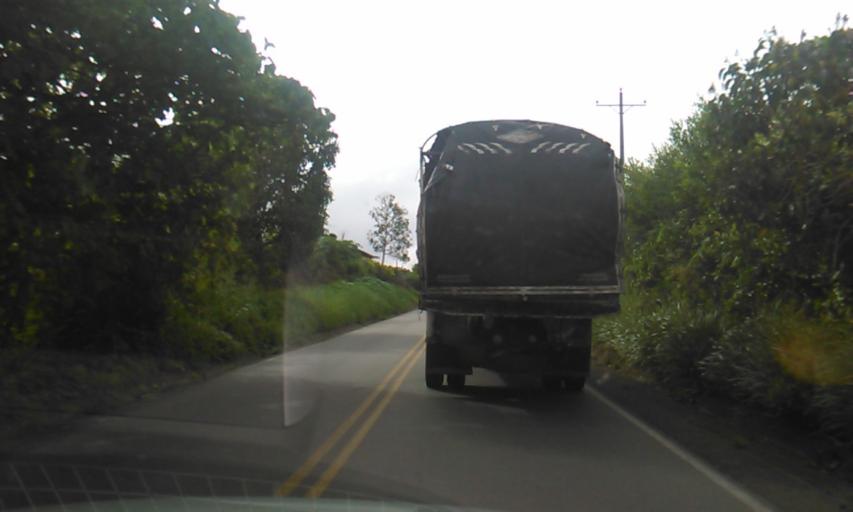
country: CO
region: Quindio
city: Cordoba
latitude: 4.4386
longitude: -75.7174
